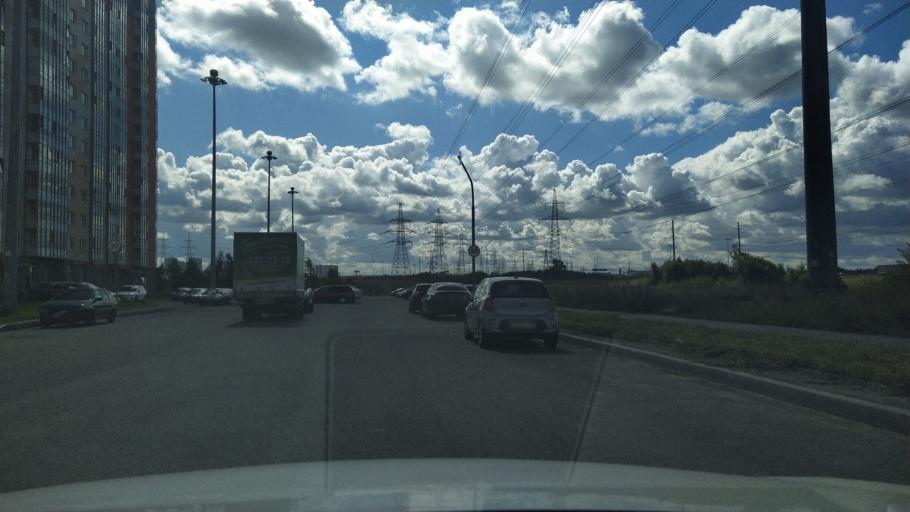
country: RU
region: Leningrad
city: Murino
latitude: 60.0266
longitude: 30.4526
